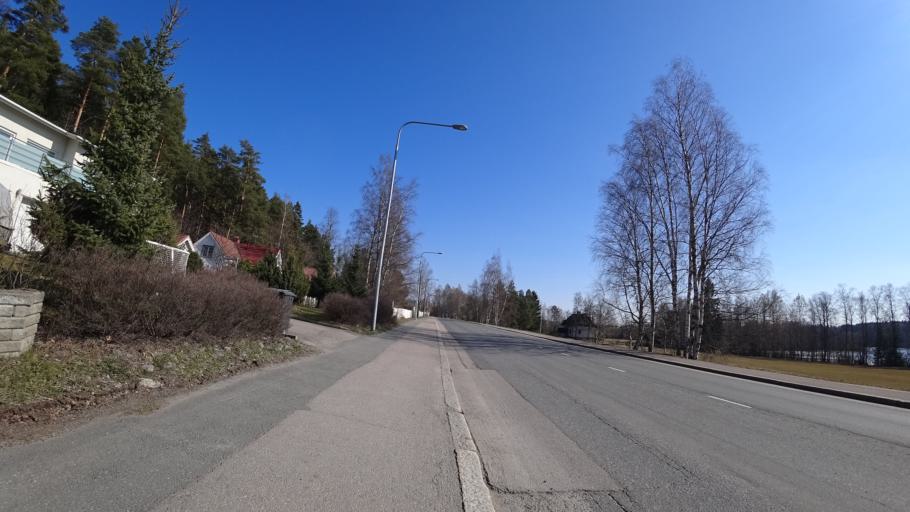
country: FI
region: Pirkanmaa
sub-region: Tampere
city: Pirkkala
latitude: 61.5152
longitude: 23.6515
